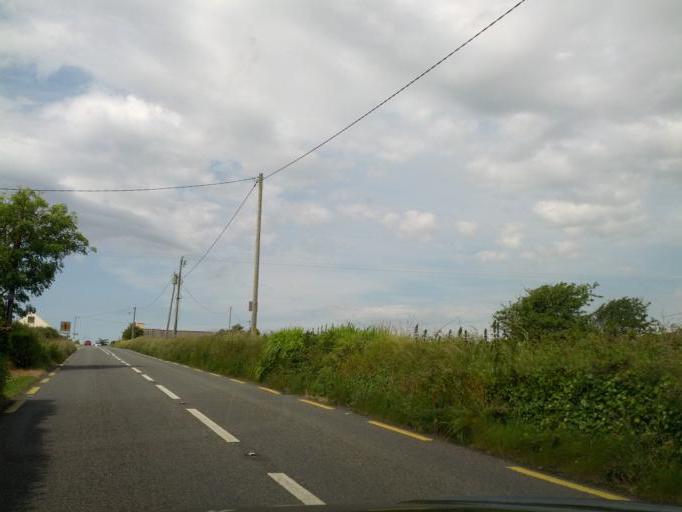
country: IE
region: Munster
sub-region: An Clar
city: Kilrush
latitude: 52.7933
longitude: -9.4438
